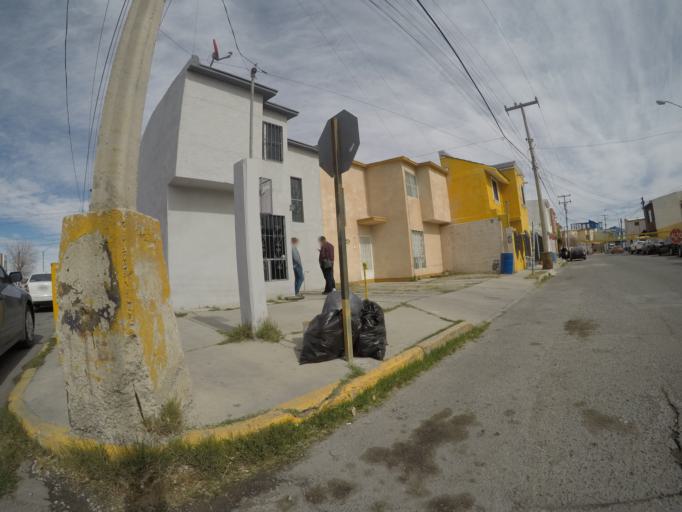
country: MX
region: Chihuahua
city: Ciudad Juarez
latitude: 31.7129
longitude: -106.4338
